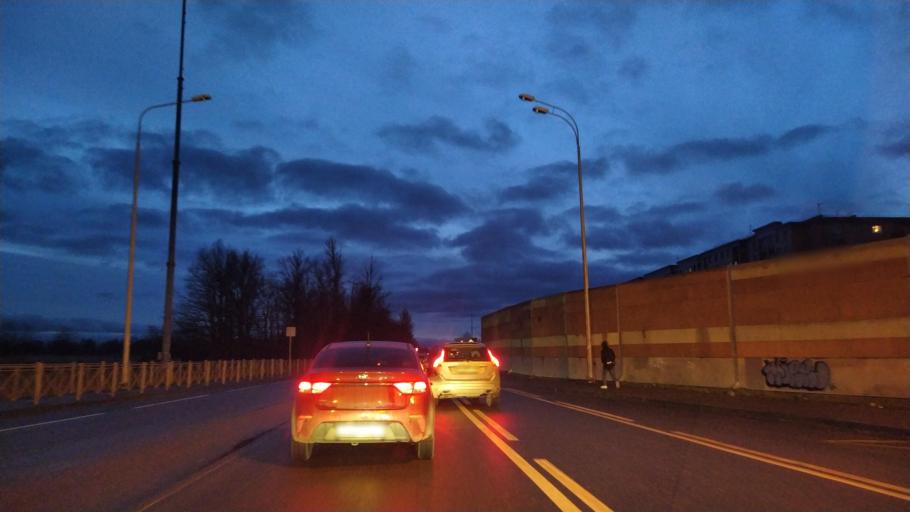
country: RU
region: St.-Petersburg
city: Tyarlevo
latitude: 59.7420
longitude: 30.4850
